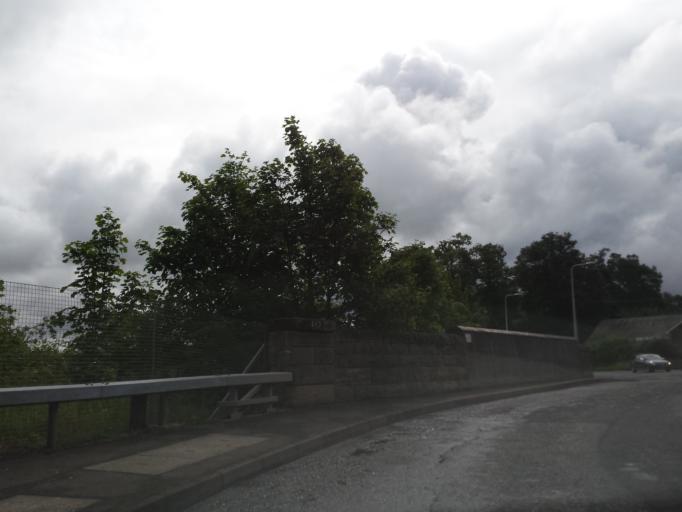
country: GB
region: Scotland
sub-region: Fife
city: Cupar
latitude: 56.3198
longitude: -3.0020
